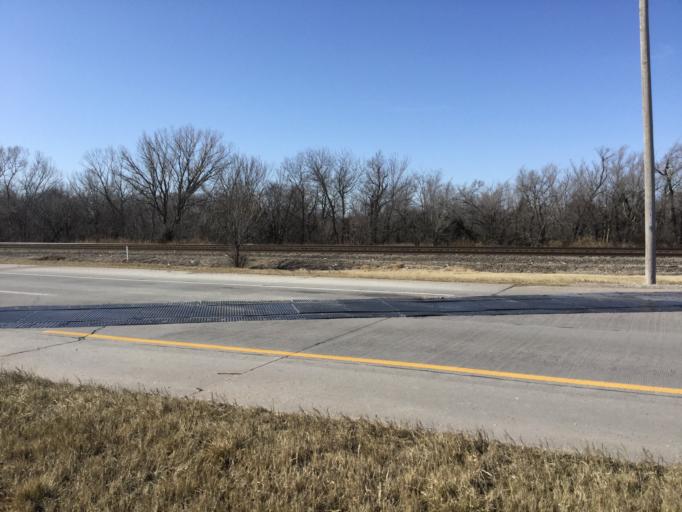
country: US
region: Kansas
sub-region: Sedgwick County
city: Derby
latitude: 37.6184
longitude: -97.2938
